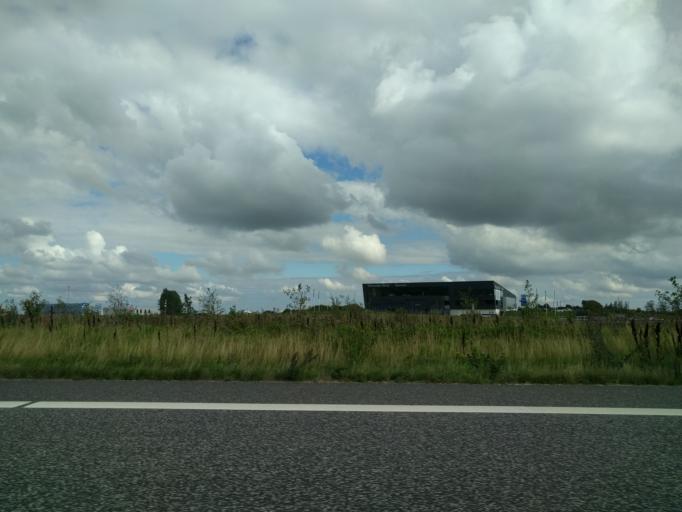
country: DK
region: South Denmark
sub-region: Vejle Kommune
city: Vejle
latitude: 55.7450
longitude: 9.5800
